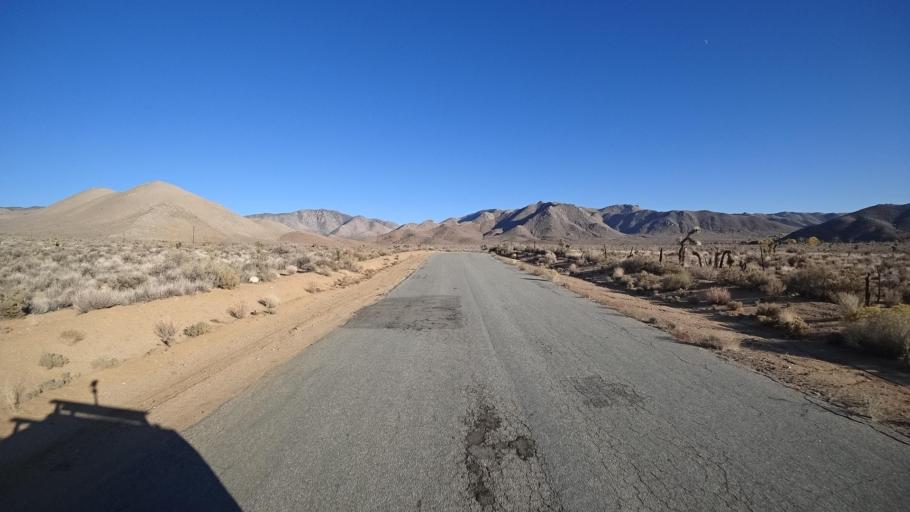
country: US
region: California
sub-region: Kern County
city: Weldon
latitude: 35.5552
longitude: -118.2174
